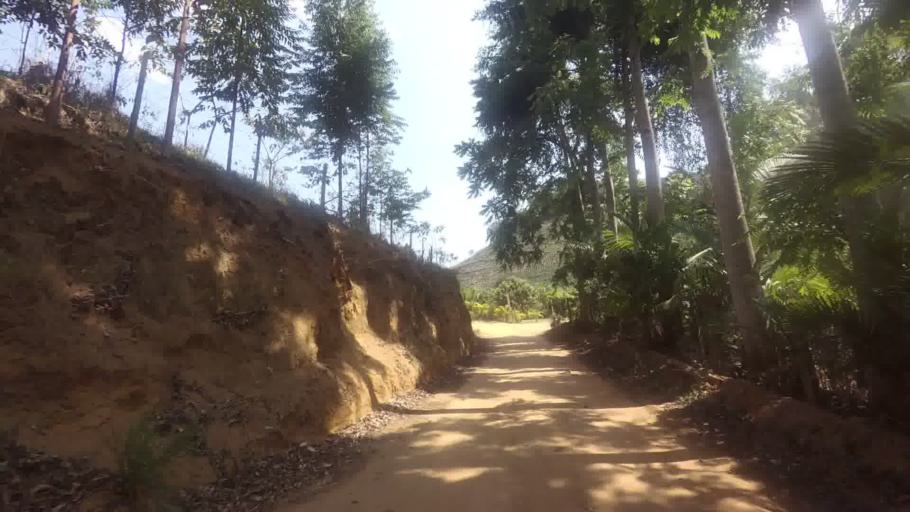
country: BR
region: Espirito Santo
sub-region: Mimoso Do Sul
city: Mimoso do Sul
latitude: -20.9893
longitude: -41.4994
